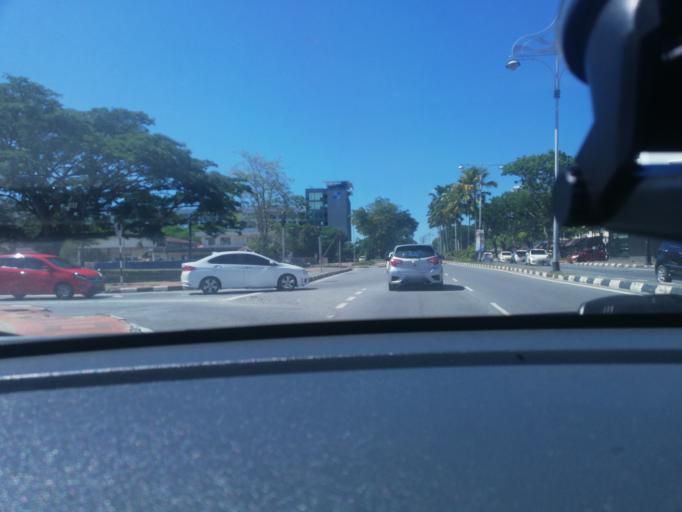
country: MY
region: Labuan
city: Victoria
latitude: 5.2791
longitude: 115.2443
